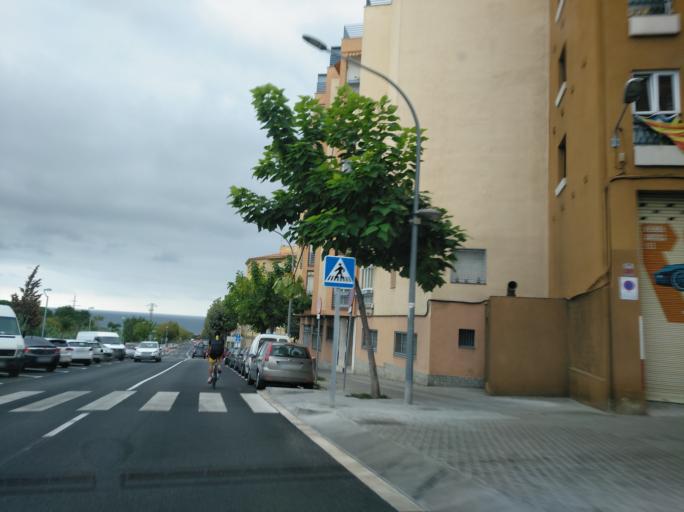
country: ES
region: Catalonia
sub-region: Provincia de Barcelona
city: Mataro
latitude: 41.5474
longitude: 2.4536
